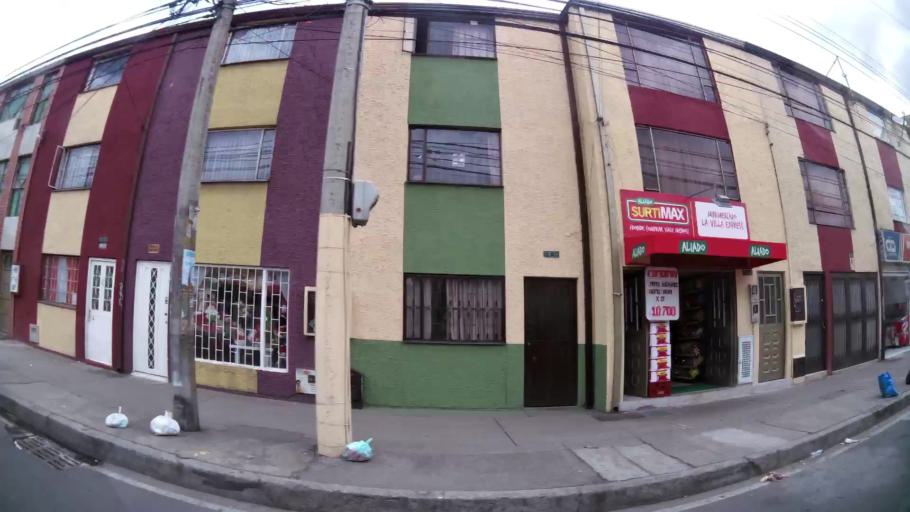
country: CO
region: Cundinamarca
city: Funza
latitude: 4.7160
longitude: -74.1208
